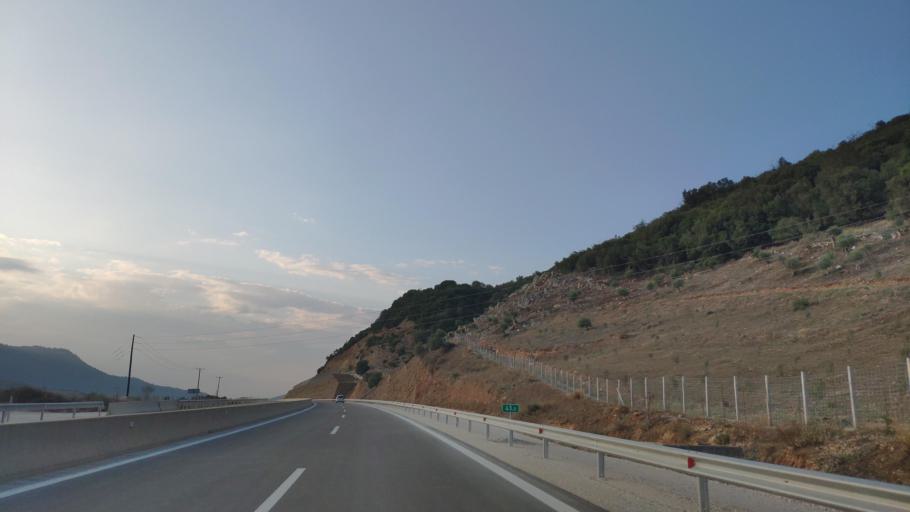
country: GR
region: West Greece
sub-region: Nomos Aitolias kai Akarnanias
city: Katouna
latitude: 38.7916
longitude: 21.1414
